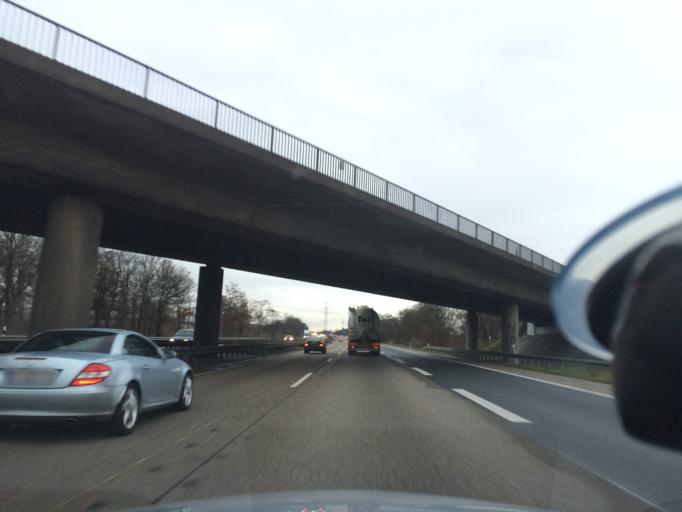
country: DE
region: Hesse
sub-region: Regierungsbezirk Darmstadt
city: Bischofsheim
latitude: 49.9731
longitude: 8.3820
